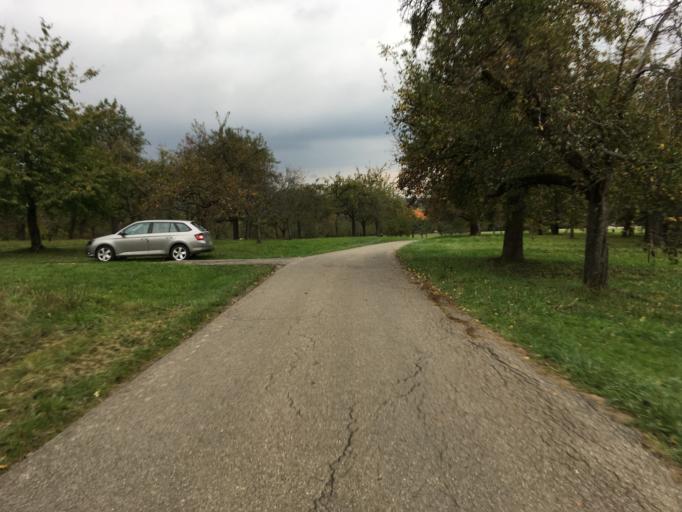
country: DE
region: Baden-Wuerttemberg
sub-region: Tuebingen Region
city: Gomaringen
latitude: 48.4447
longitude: 9.0933
